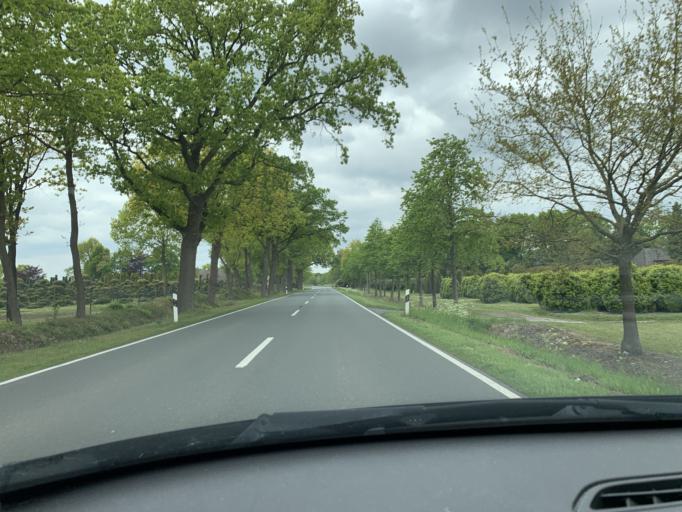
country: DE
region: Lower Saxony
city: Bad Zwischenahn
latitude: 53.1868
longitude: 8.0611
